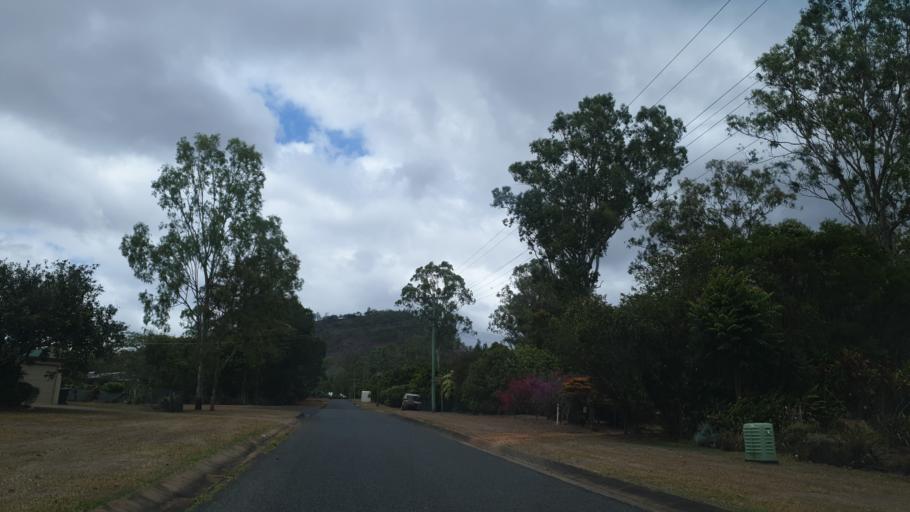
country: AU
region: Queensland
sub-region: Tablelands
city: Tolga
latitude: -17.2082
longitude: 145.4387
